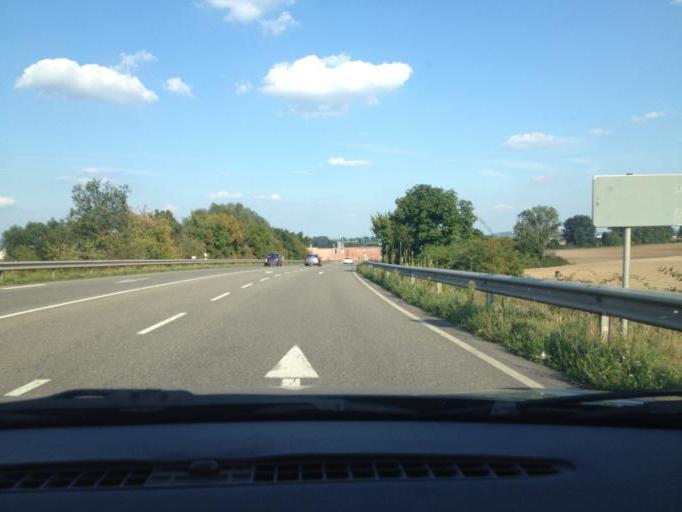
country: DE
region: Baden-Wuerttemberg
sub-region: Karlsruhe Region
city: Neulussheim
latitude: 49.3075
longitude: 8.5354
